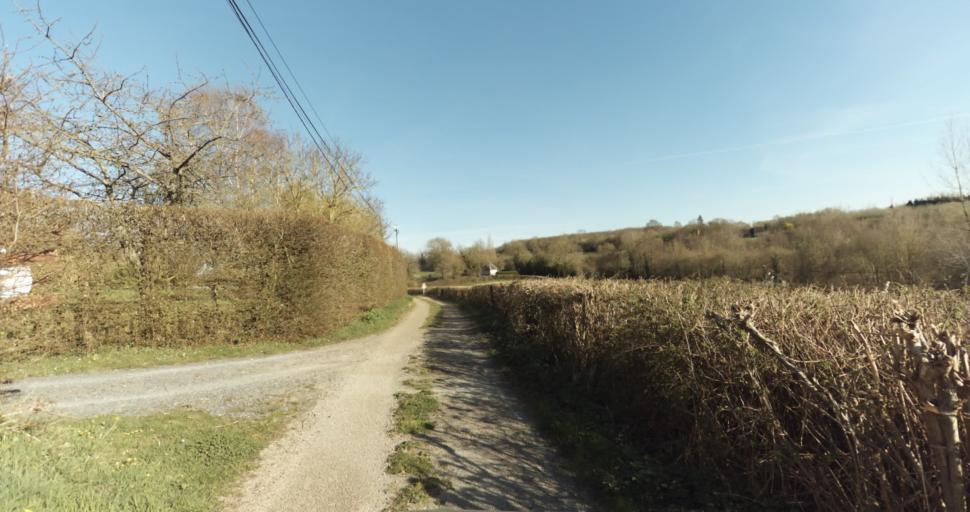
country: FR
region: Lower Normandy
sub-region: Departement du Calvados
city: Livarot
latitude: 49.0088
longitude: 0.0952
